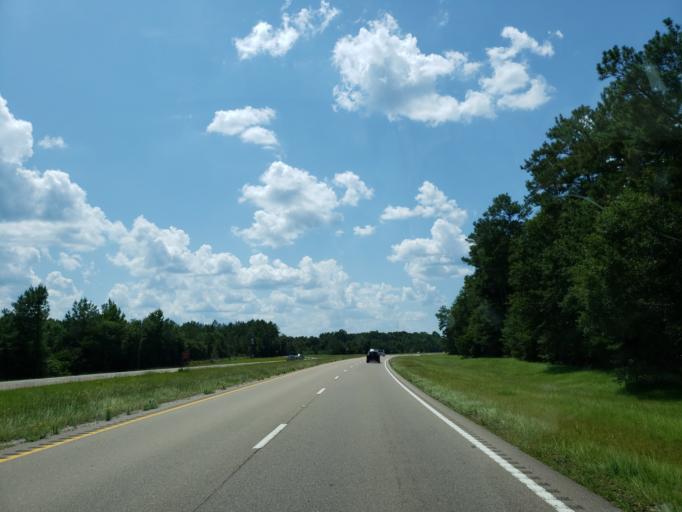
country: US
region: Mississippi
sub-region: Perry County
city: New Augusta
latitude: 31.1446
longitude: -88.8771
